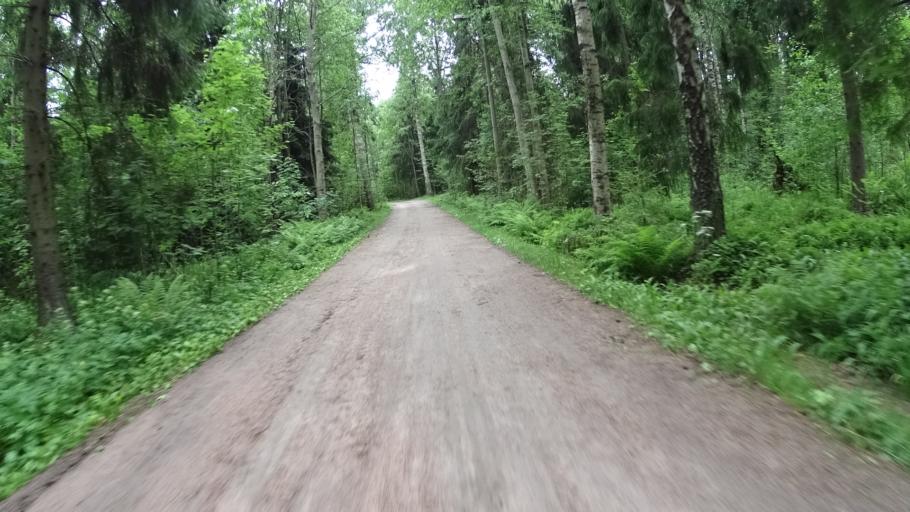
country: FI
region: Uusimaa
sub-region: Helsinki
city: Helsinki
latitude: 60.2602
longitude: 24.9106
